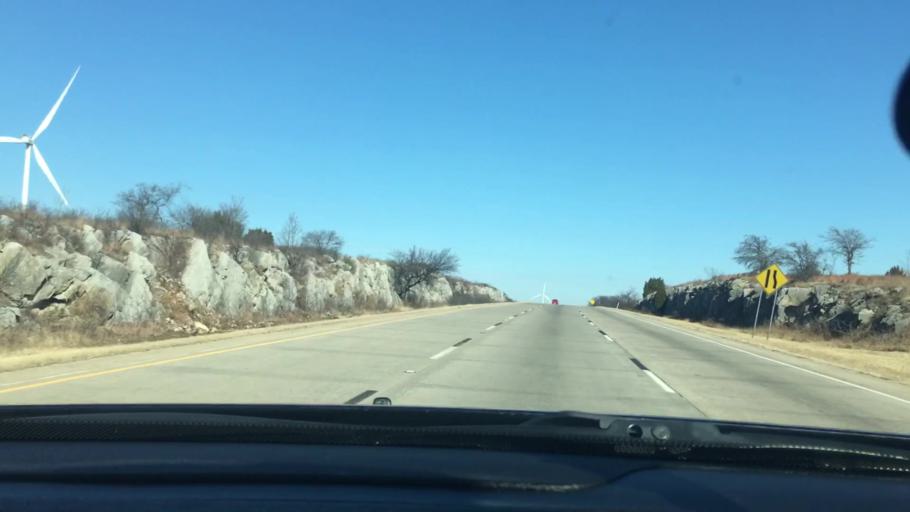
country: US
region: Oklahoma
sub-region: Murray County
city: Davis
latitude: 34.3749
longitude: -97.1446
